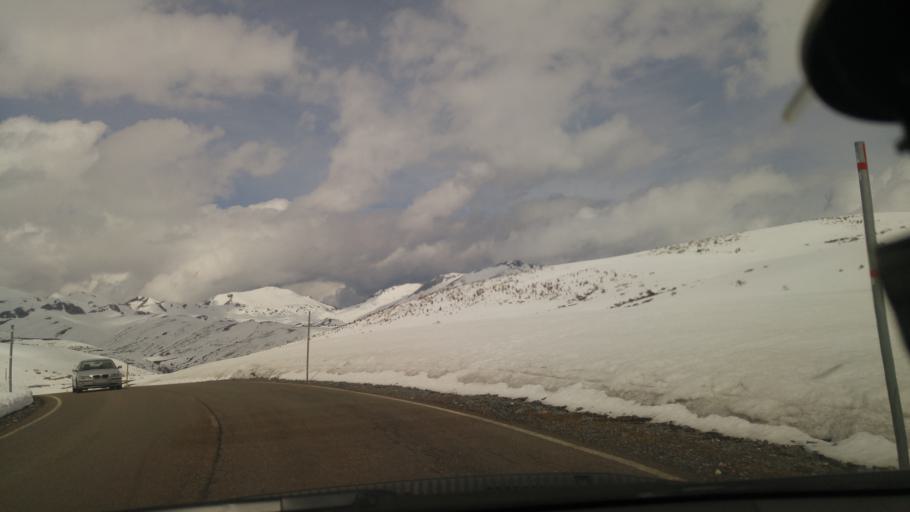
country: ES
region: Castille and Leon
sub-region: Provincia de Leon
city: Puebla de Lillo
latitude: 43.0475
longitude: -5.3769
